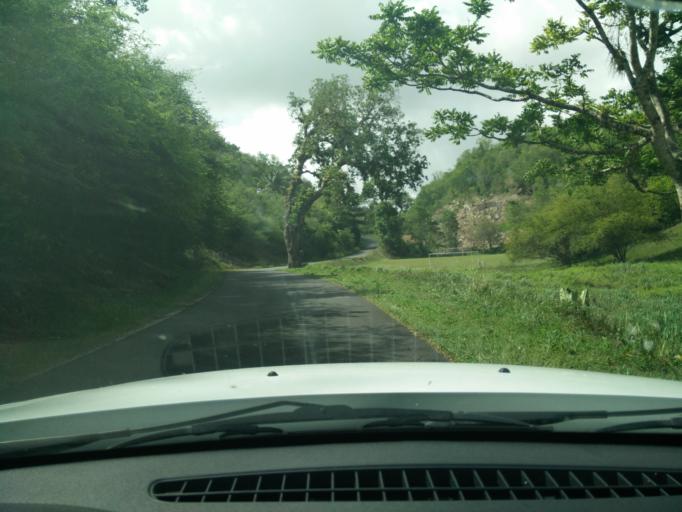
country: GP
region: Guadeloupe
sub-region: Guadeloupe
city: Le Gosier
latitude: 16.2264
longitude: -61.4570
